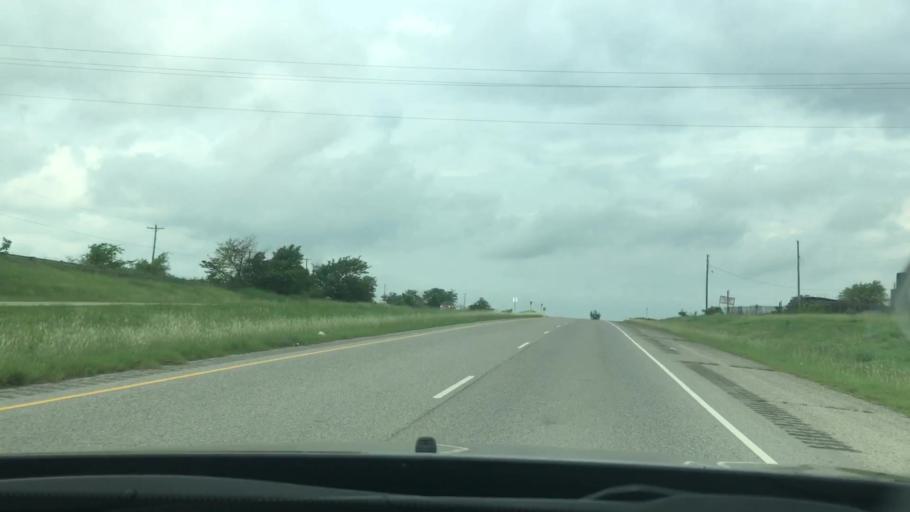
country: US
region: Oklahoma
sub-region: Carter County
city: Wilson
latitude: 34.1731
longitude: -97.4612
